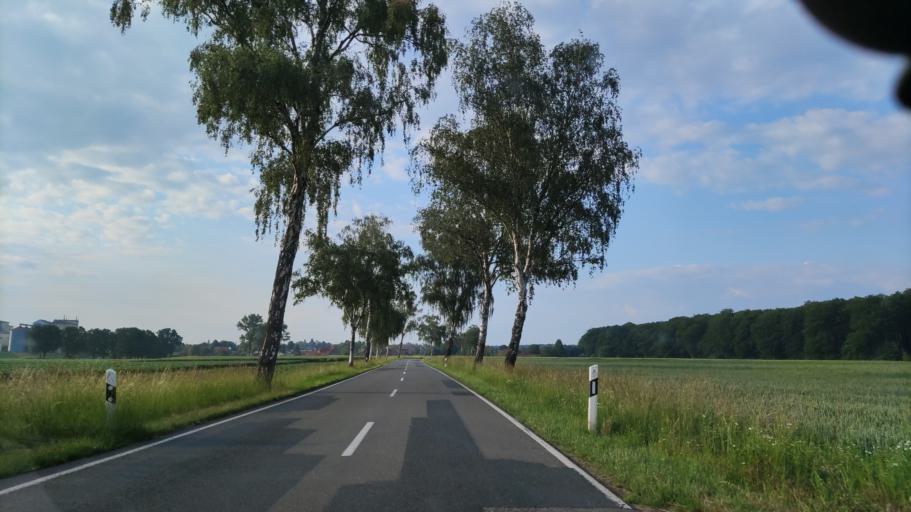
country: DE
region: Lower Saxony
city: Ebstorf
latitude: 53.0104
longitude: 10.4185
